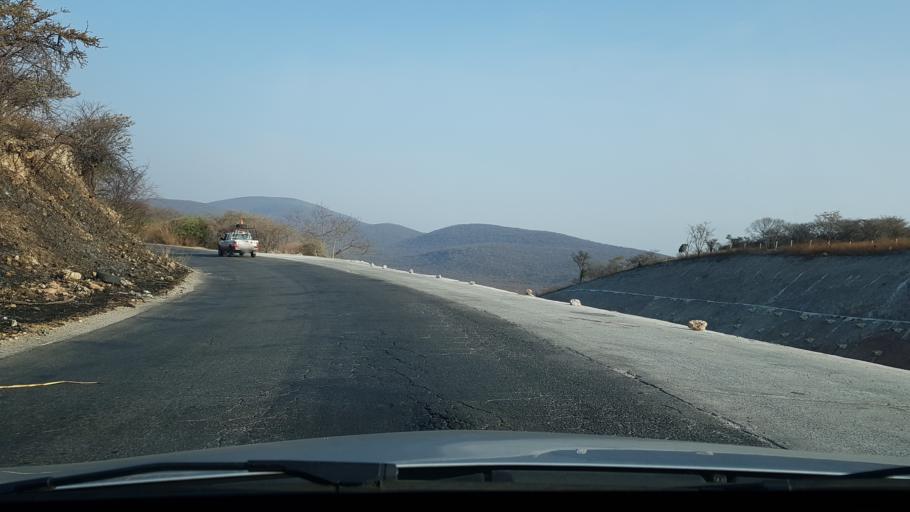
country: MX
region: Morelos
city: Tlaltizapan
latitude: 18.6630
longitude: -99.0461
